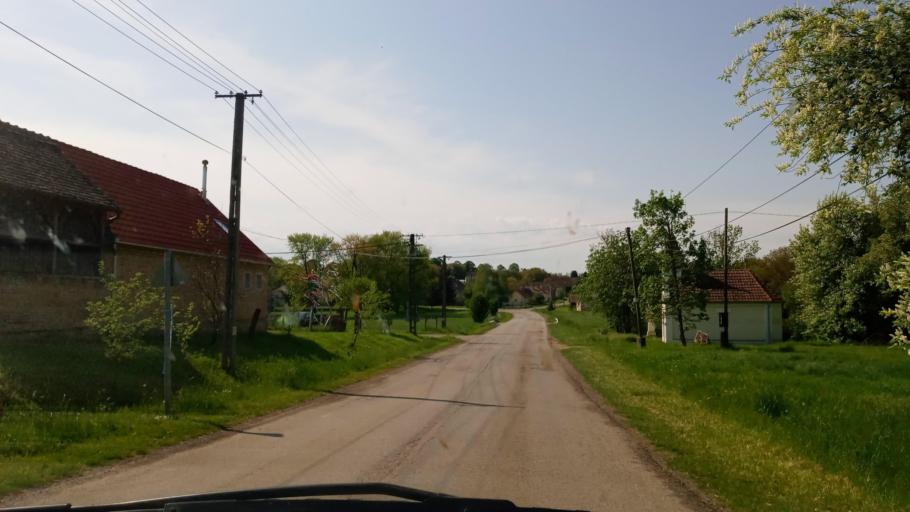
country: HU
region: Baranya
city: Boly
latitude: 45.9489
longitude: 18.5728
